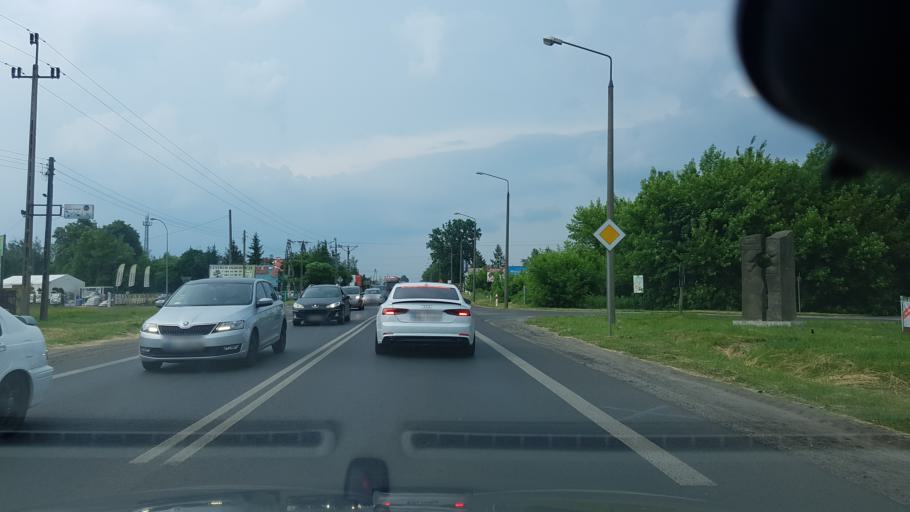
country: PL
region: Masovian Voivodeship
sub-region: Powiat legionowski
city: Michalow-Reginow
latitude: 52.4139
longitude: 20.9621
